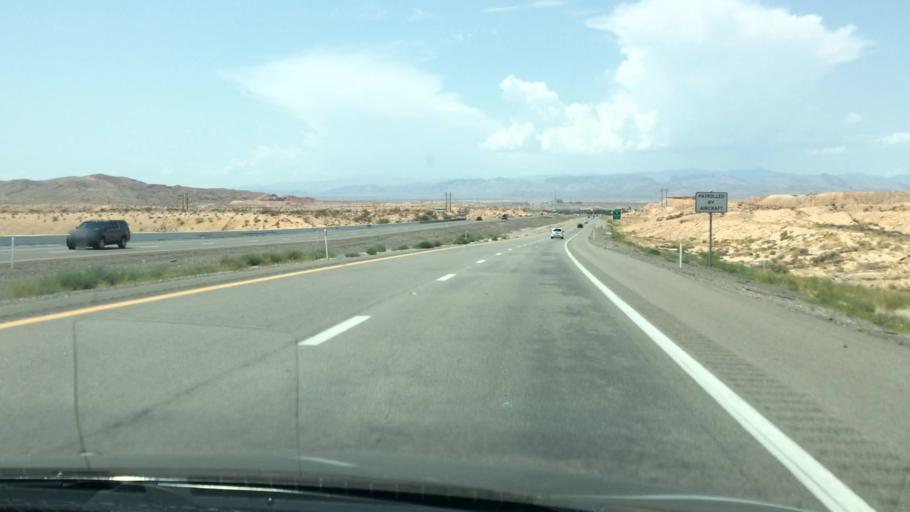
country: US
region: Nevada
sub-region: Clark County
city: Moapa Town
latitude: 36.6679
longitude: -114.5358
